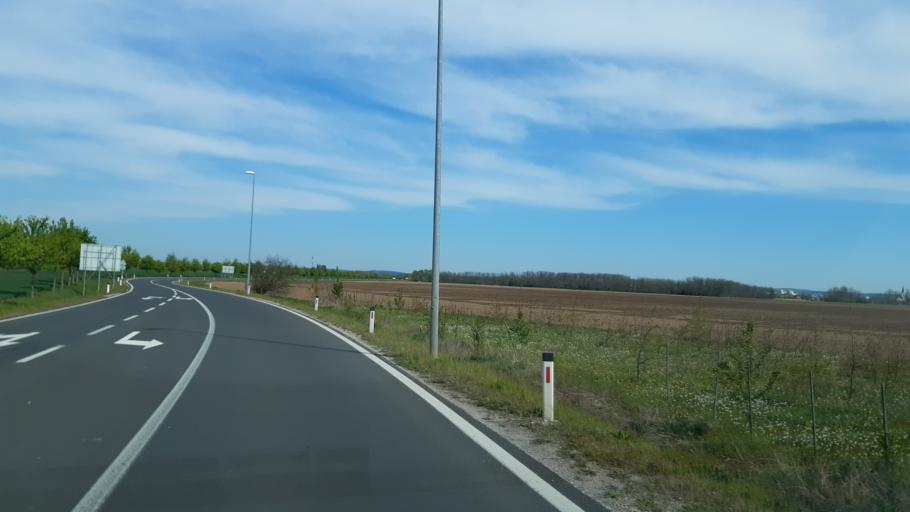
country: SI
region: Murska Sobota
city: Krog
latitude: 46.6362
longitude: 16.1572
